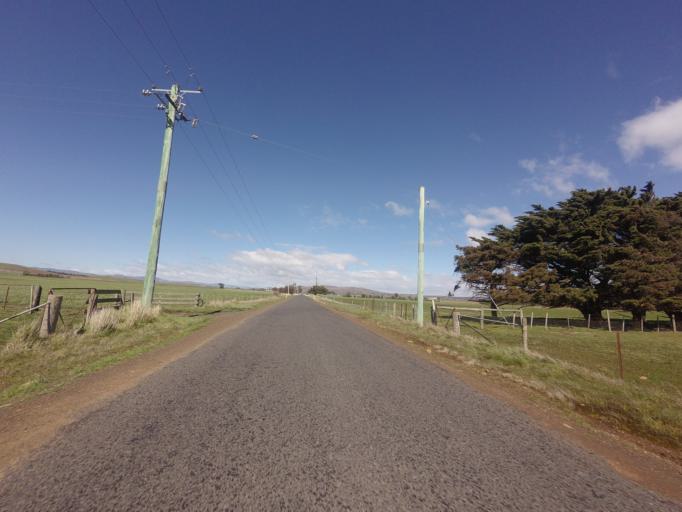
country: AU
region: Tasmania
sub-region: Northern Midlands
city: Evandale
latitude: -41.9938
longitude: 147.4536
